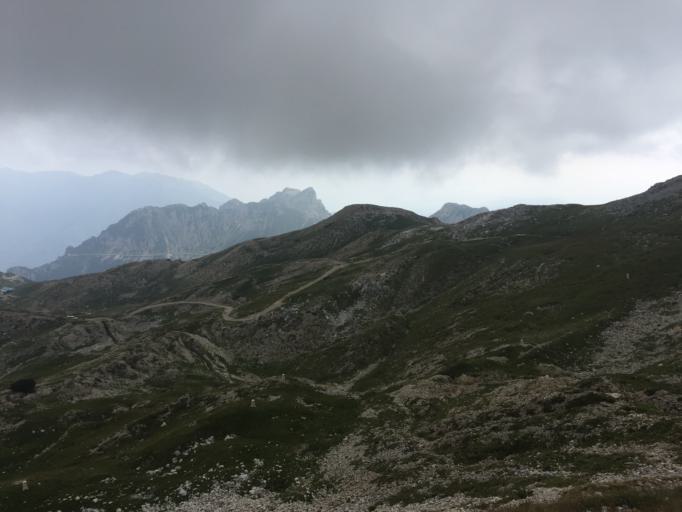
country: IT
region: Trentino-Alto Adige
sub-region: Provincia di Trento
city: Vallarsa
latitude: 45.7940
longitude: 11.1767
